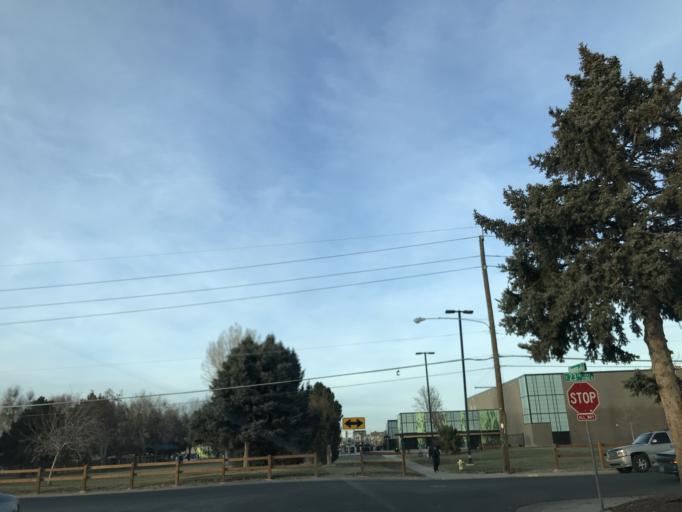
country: US
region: Colorado
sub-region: Adams County
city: Aurora
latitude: 39.7509
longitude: -104.8658
